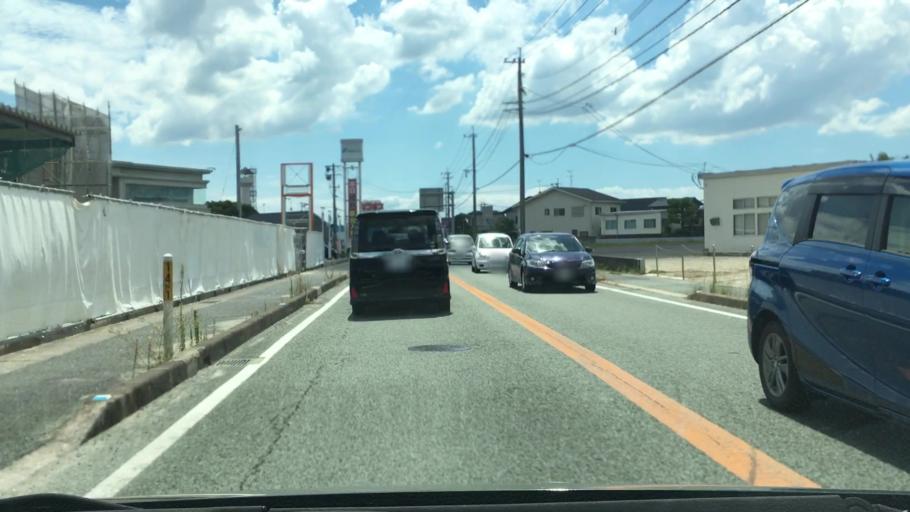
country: JP
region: Saga Prefecture
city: Kanzakimachi-kanzaki
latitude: 33.3307
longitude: 130.4123
